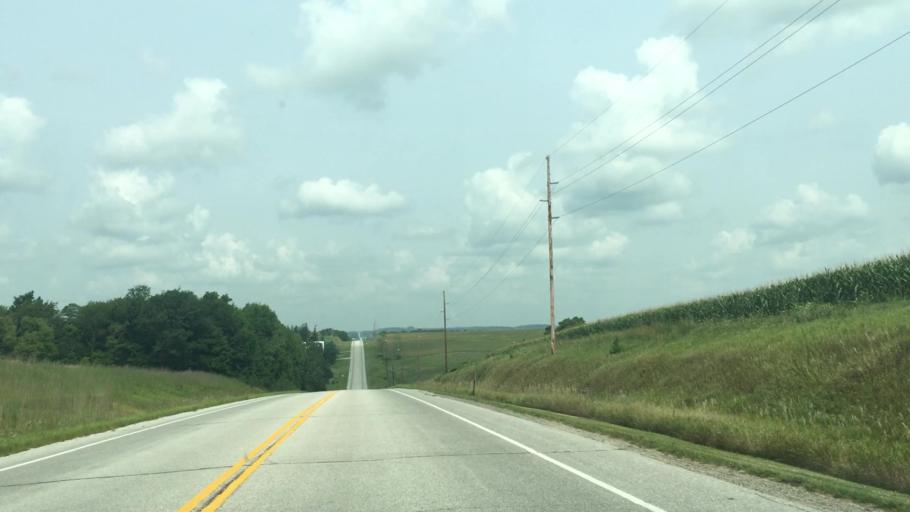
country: US
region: Minnesota
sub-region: Fillmore County
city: Harmony
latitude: 43.5714
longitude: -91.9298
